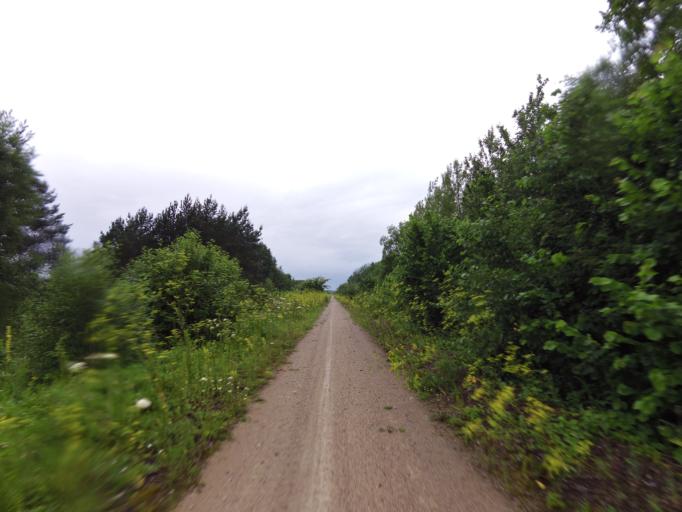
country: EE
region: Laeaene
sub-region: Ridala Parish
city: Uuemoisa
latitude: 58.9524
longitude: 23.7947
